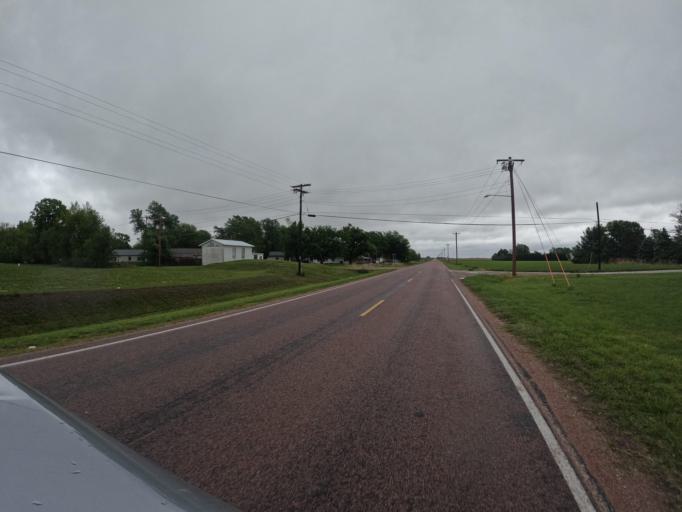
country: US
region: Nebraska
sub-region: Clay County
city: Harvard
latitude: 40.6259
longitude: -98.0948
